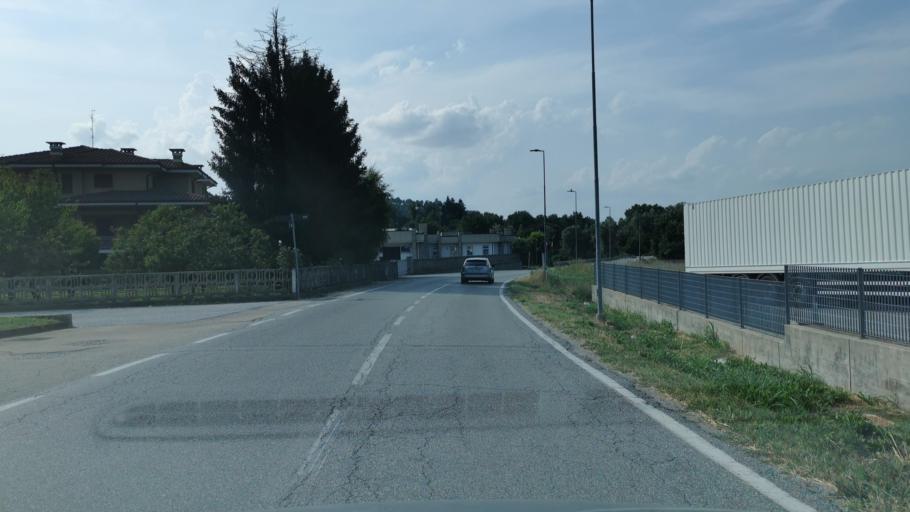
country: IT
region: Piedmont
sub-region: Provincia di Cuneo
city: Cherasco
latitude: 44.6463
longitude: 7.8764
